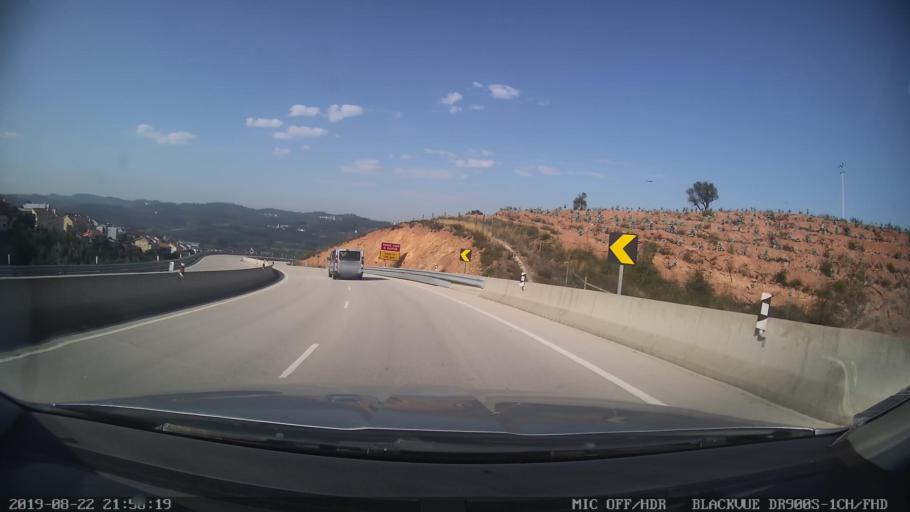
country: PT
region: Coimbra
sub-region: Coimbra
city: Coimbra
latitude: 40.1785
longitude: -8.3871
